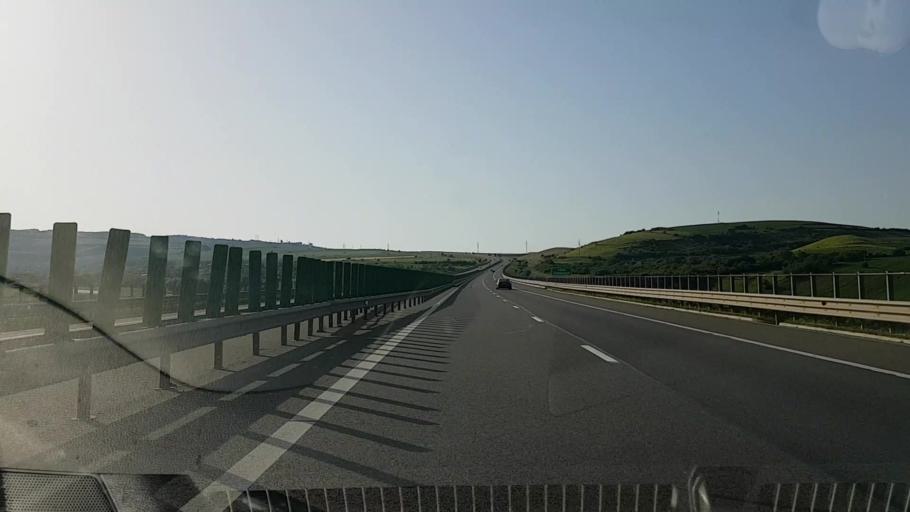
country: RO
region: Cluj
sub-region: Comuna Sandulesti
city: Copaceni
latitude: 46.5740
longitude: 23.7449
